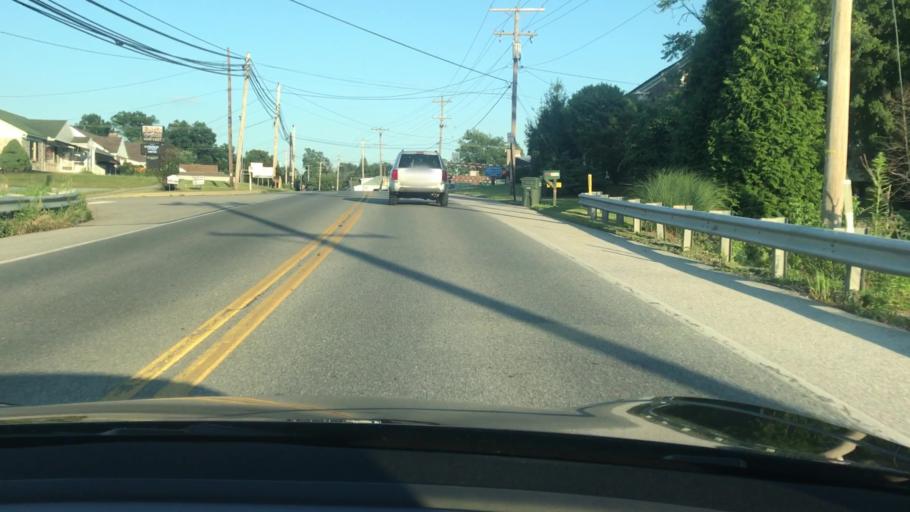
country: US
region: Pennsylvania
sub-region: York County
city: Weigelstown
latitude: 39.9897
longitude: -76.8380
